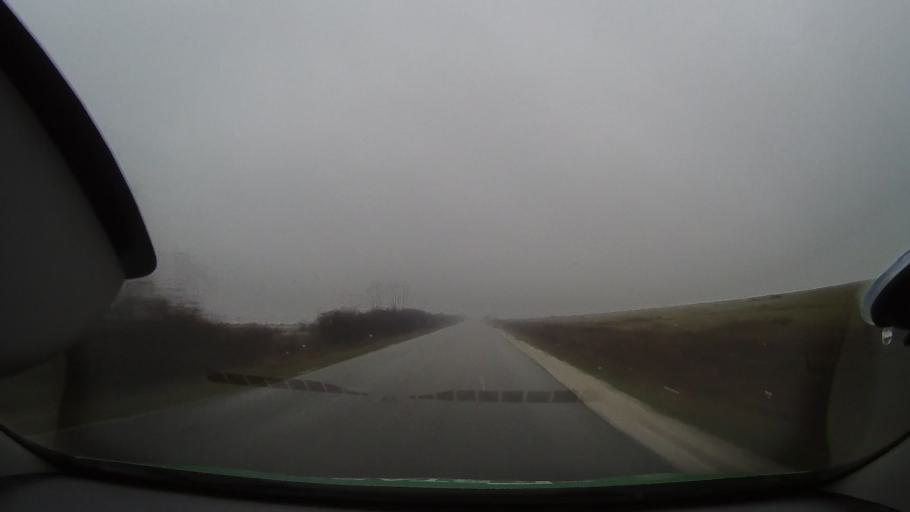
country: RO
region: Arad
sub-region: Comuna Craiova
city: Craiova
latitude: 46.6104
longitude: 21.9568
